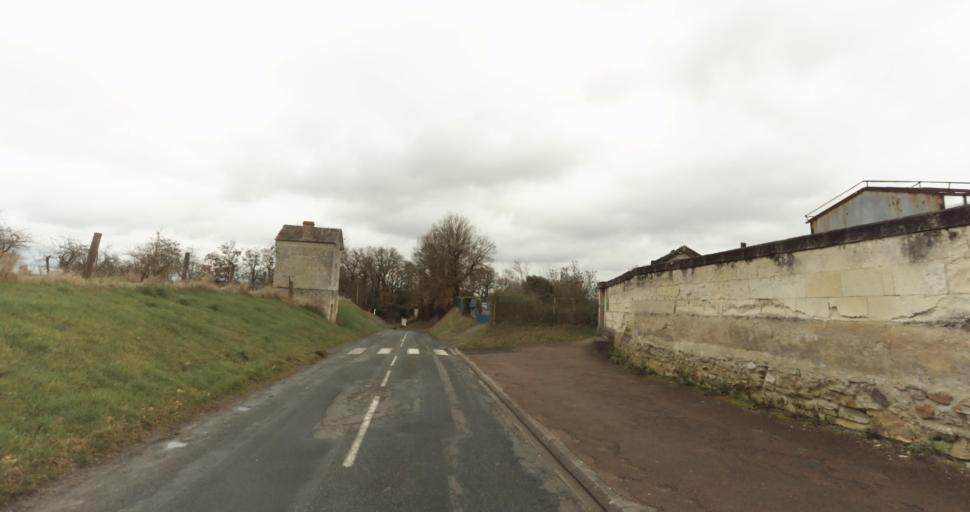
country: FR
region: Pays de la Loire
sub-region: Departement de Maine-et-Loire
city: Distre
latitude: 47.2451
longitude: -0.1011
